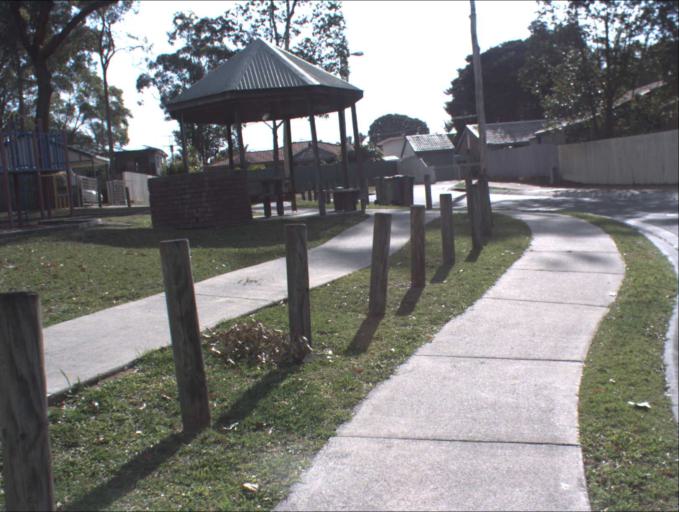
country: AU
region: Queensland
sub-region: Logan
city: Waterford West
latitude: -27.6700
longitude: 153.1260
